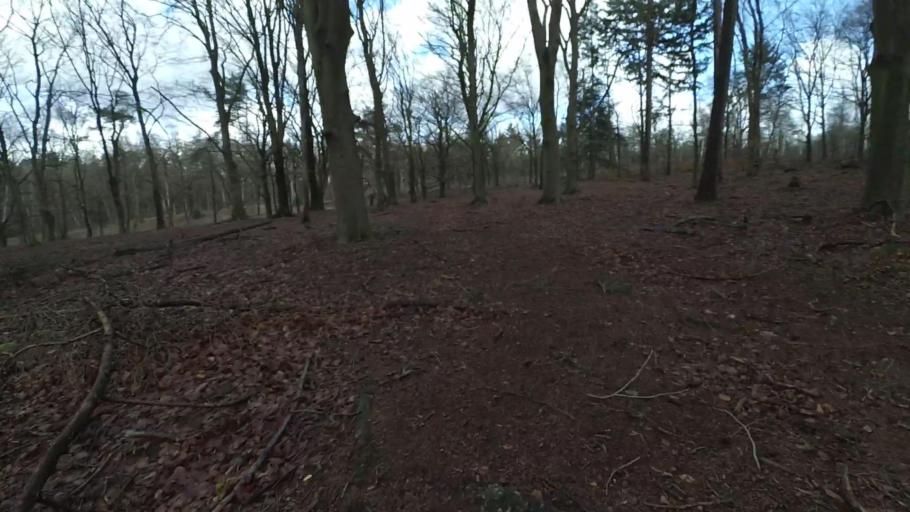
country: NL
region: Utrecht
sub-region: Gemeente Utrechtse Heuvelrug
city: Doorn
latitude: 52.0506
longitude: 5.3419
